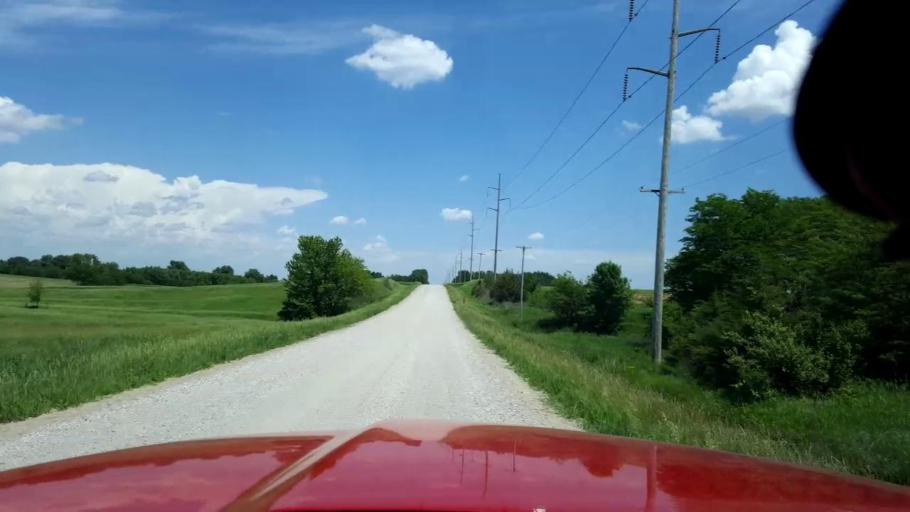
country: US
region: Iowa
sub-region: Story County
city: Gilbert
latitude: 42.0492
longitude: -93.7523
